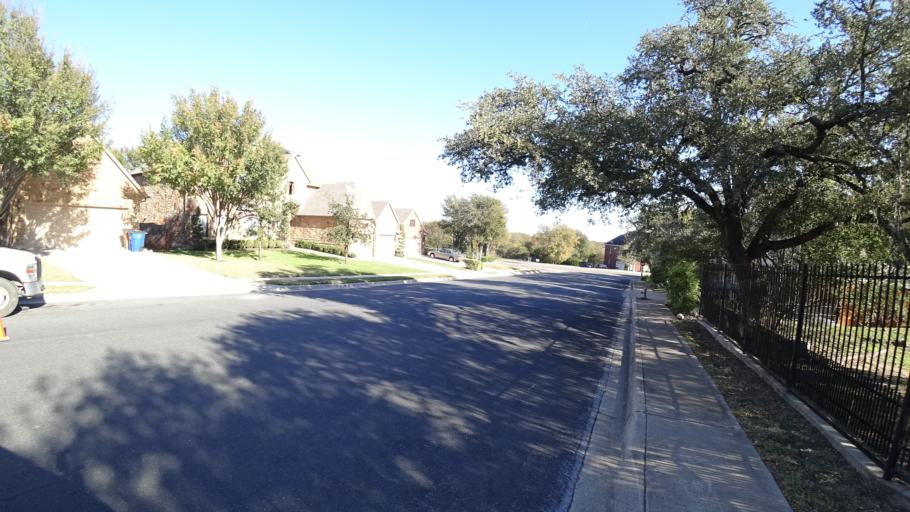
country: US
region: Texas
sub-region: Williamson County
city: Jollyville
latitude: 30.4223
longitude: -97.7789
